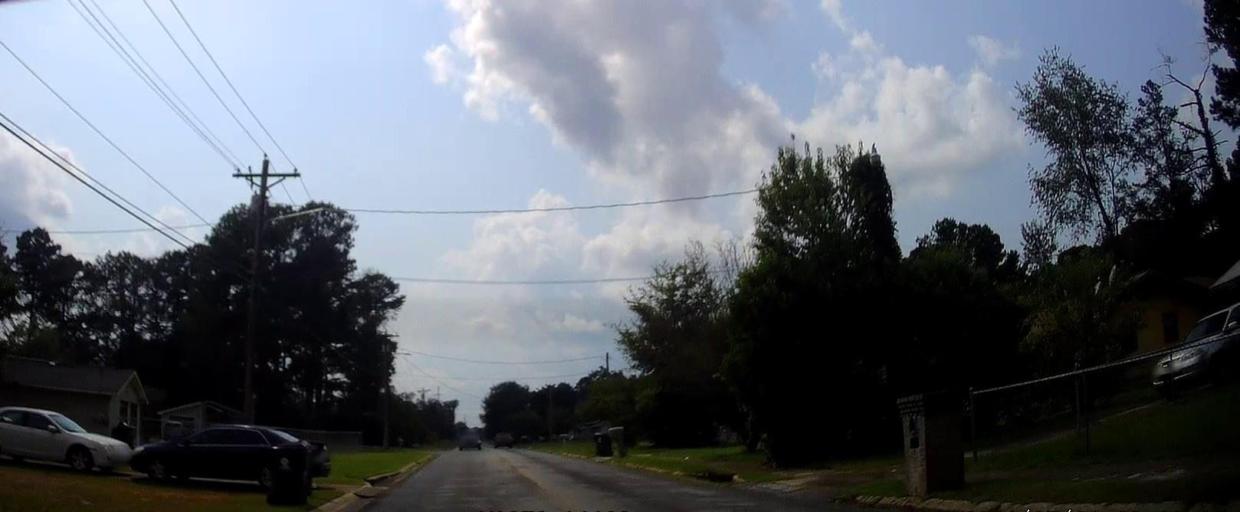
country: US
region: Georgia
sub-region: Houston County
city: Warner Robins
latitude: 32.6485
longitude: -83.6166
